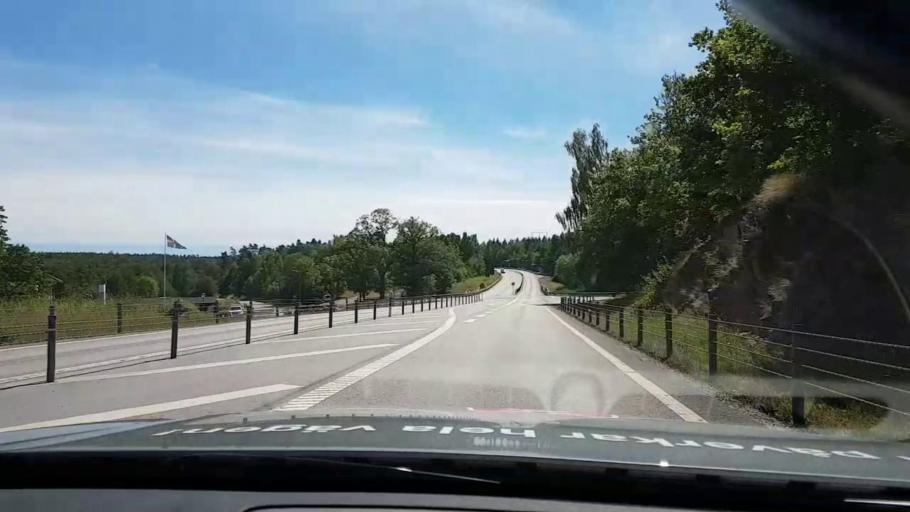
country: SE
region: Kalmar
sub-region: Vasterviks Kommun
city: Gamleby
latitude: 57.8343
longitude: 16.4423
